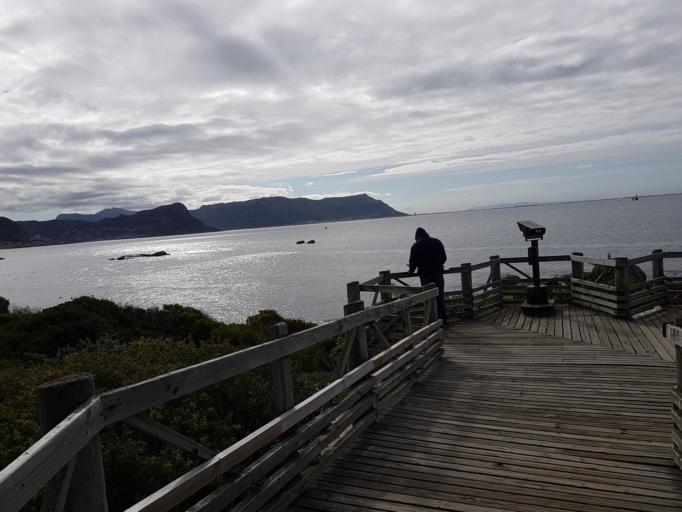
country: ZA
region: Western Cape
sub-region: City of Cape Town
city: Retreat
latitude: -34.1955
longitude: 18.4499
